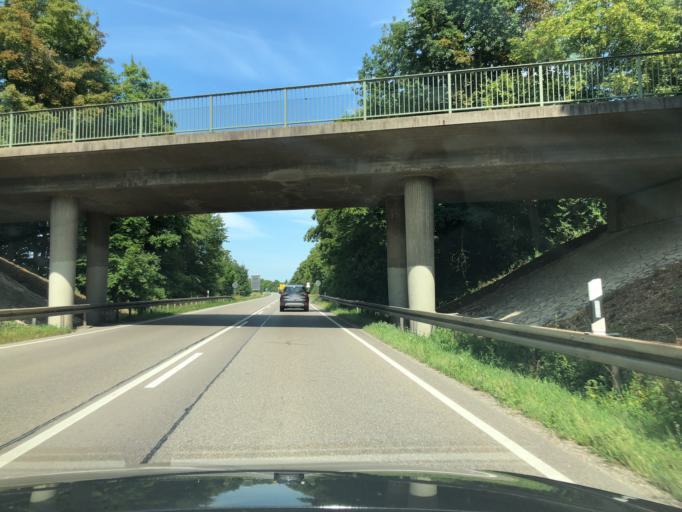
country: DE
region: Bavaria
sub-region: Upper Bavaria
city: Manching
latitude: 48.7124
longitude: 11.4747
